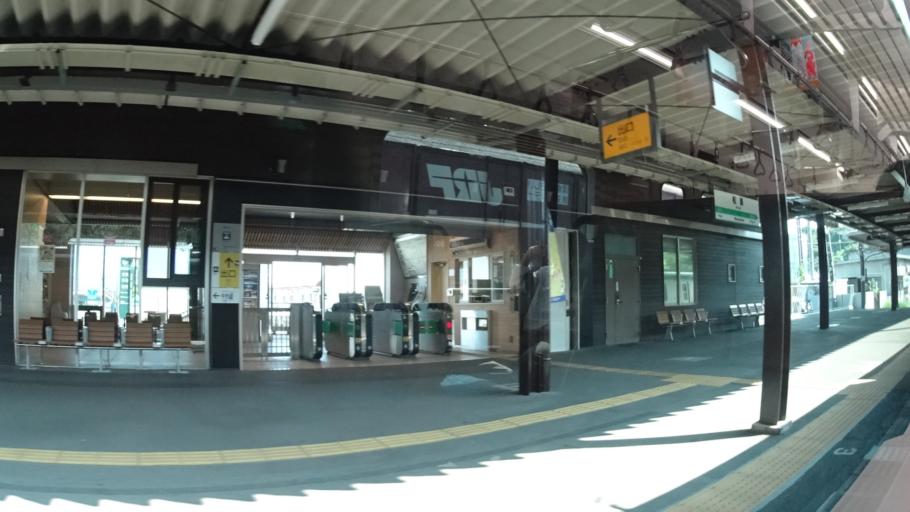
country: JP
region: Miyagi
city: Matsushima
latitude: 38.3801
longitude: 141.0662
